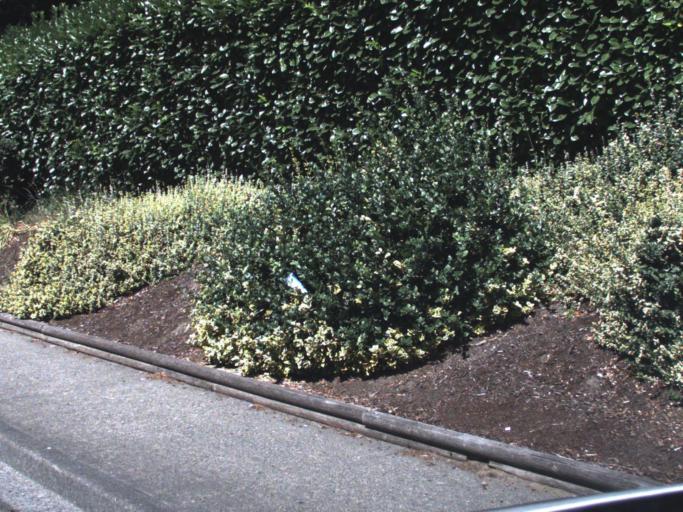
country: US
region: Washington
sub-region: King County
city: Newcastle
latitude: 47.5045
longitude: -122.1604
